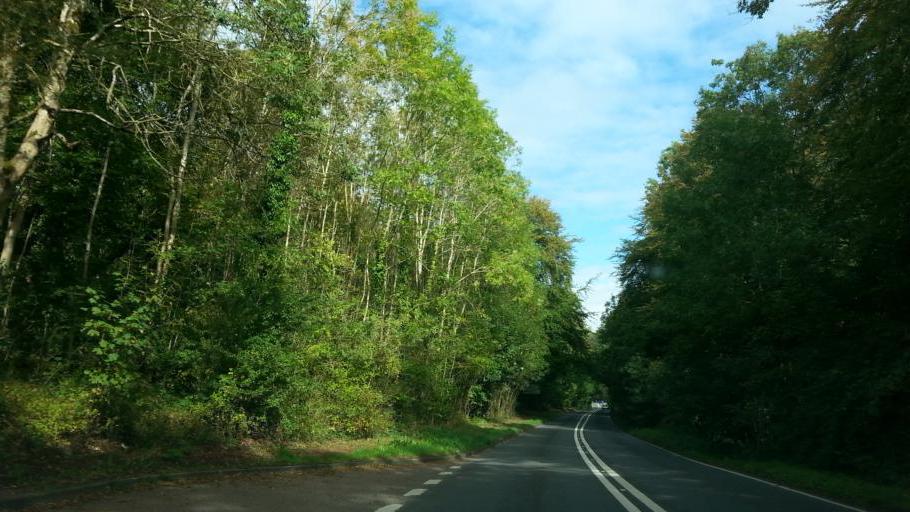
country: GB
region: England
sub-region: Gloucestershire
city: Painswick
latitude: 51.8130
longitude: -2.1770
